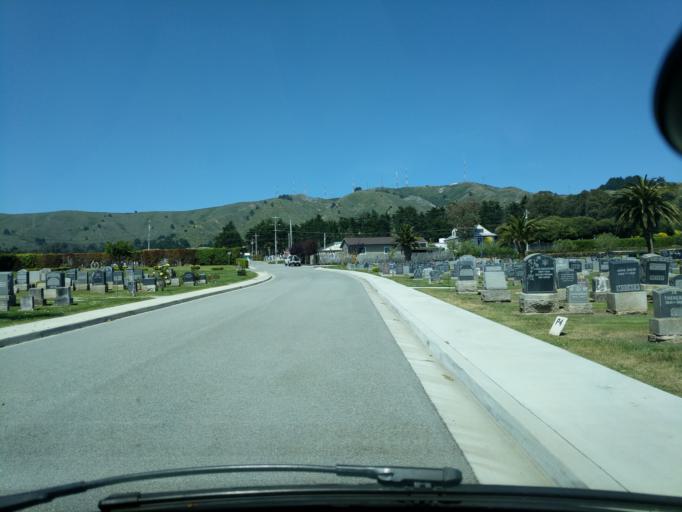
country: US
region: California
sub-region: San Mateo County
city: Colma
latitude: 37.6784
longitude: -122.4510
